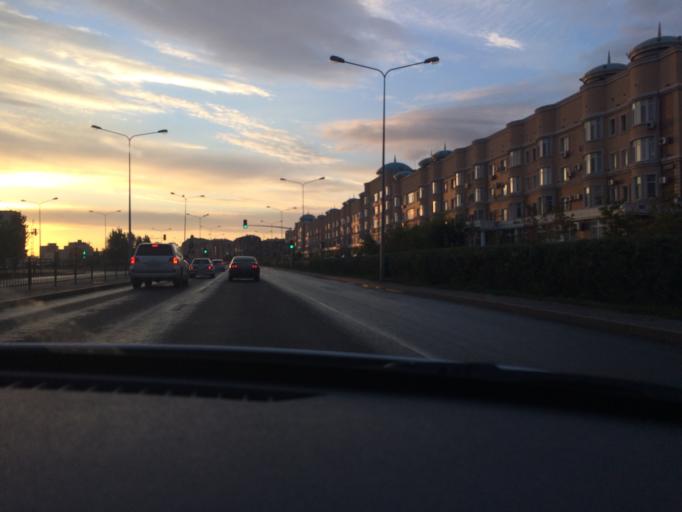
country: KZ
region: Astana Qalasy
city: Astana
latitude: 51.1479
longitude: 71.3939
